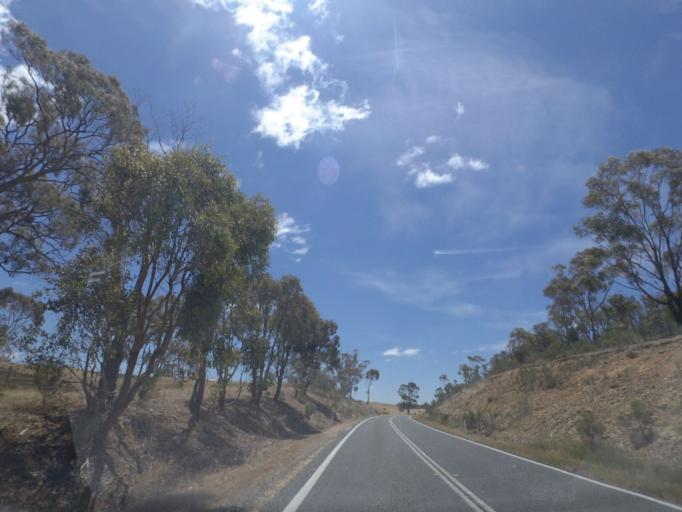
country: AU
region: Victoria
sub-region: Mount Alexander
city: Castlemaine
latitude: -37.2147
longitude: 144.1402
